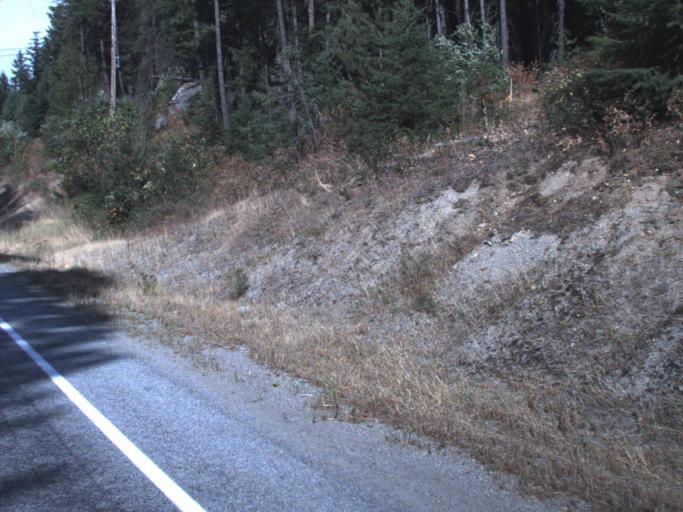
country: US
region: Washington
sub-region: Pend Oreille County
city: Newport
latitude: 48.1611
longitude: -117.3017
